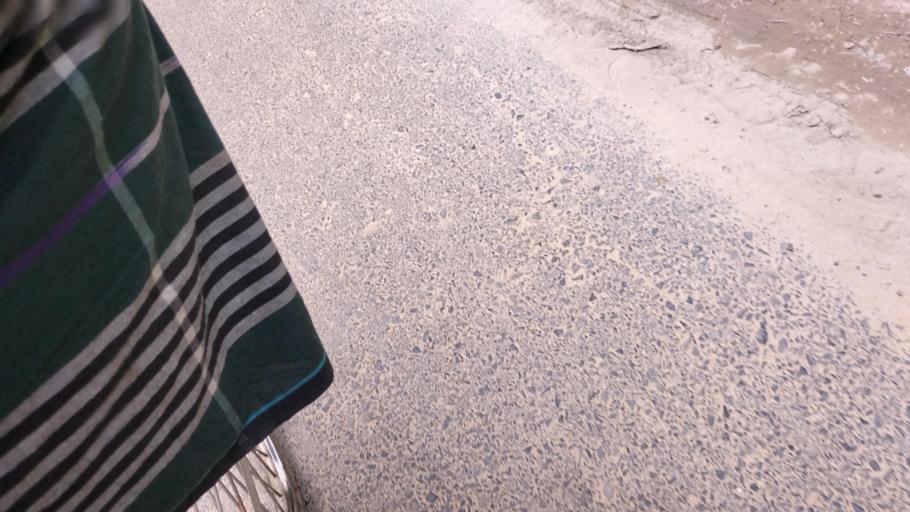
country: BD
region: Rajshahi
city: Rajshahi
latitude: 24.5172
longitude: 88.6240
